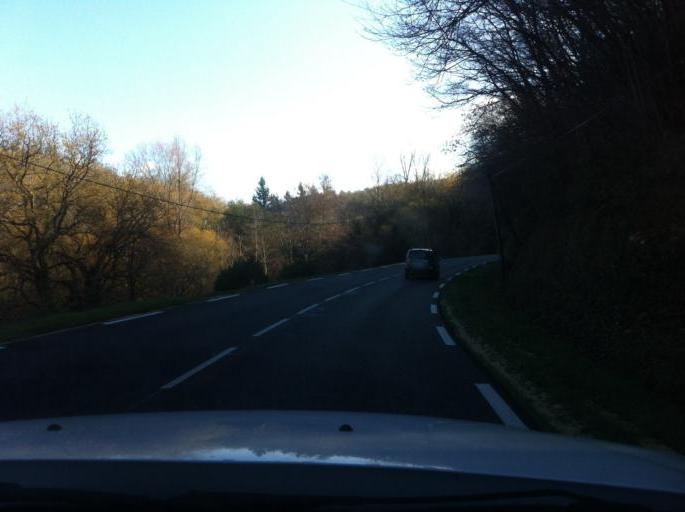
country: FR
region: Aquitaine
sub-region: Departement de la Dordogne
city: Rouffignac-Saint-Cernin-de-Reilhac
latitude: 45.0324
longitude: 0.9003
